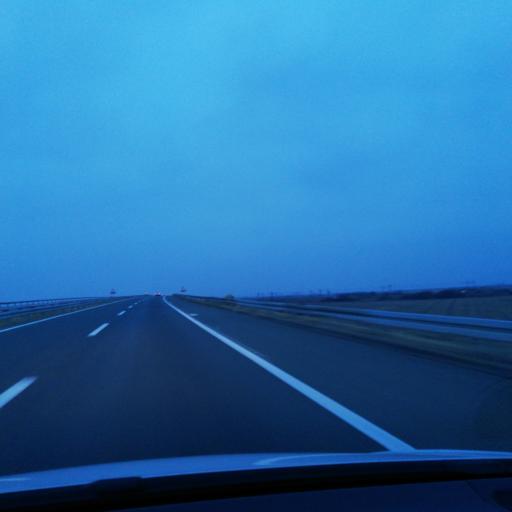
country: RS
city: Sasinci
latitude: 44.9910
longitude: 19.7062
